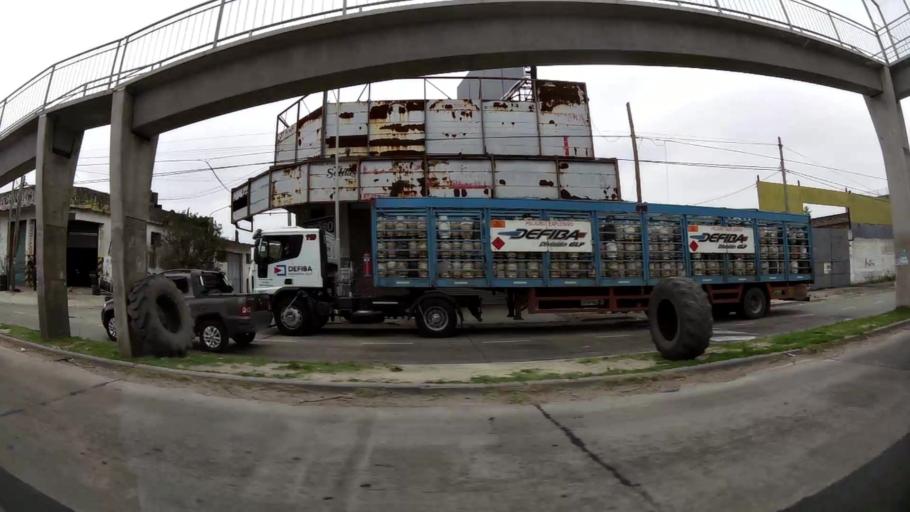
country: AR
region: Buenos Aires
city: San Justo
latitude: -34.6980
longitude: -58.5440
